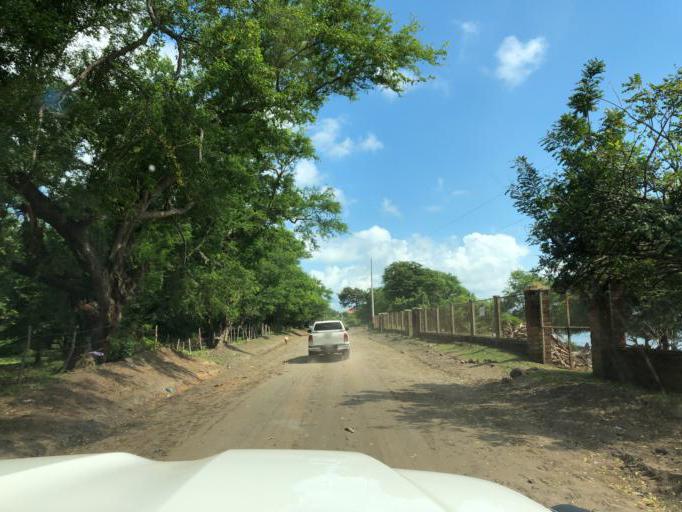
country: NI
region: Granada
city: Granada
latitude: 12.0067
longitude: -85.9331
